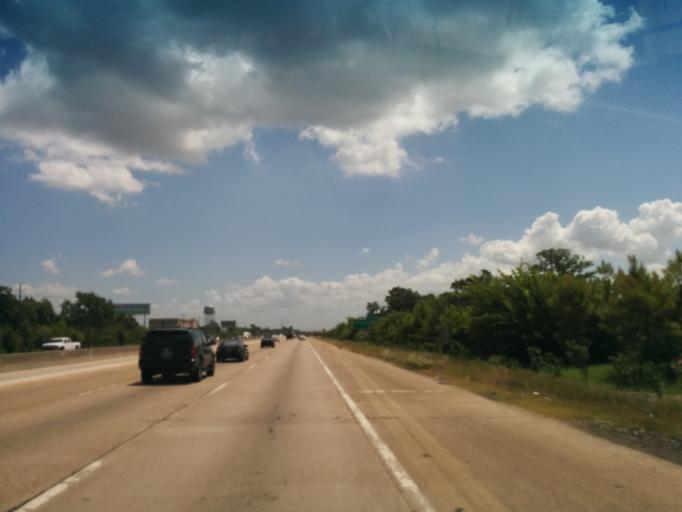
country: US
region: Texas
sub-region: Harris County
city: Channelview
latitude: 29.7818
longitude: -95.1143
